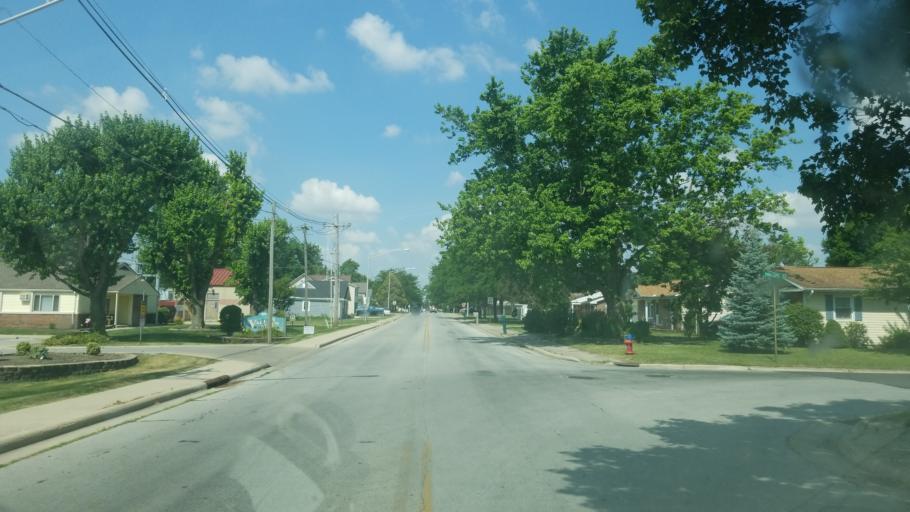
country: US
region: Ohio
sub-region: Auglaize County
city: Wapakoneta
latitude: 40.5700
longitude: -84.1780
